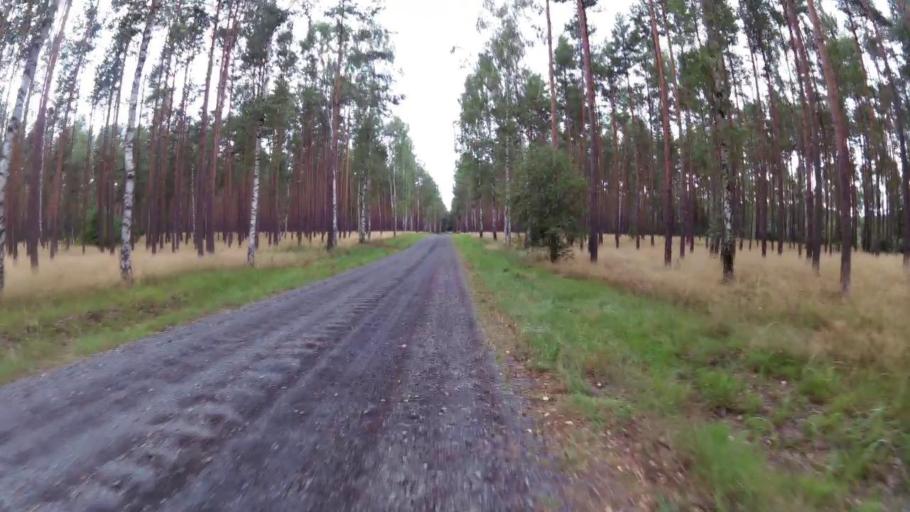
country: PL
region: West Pomeranian Voivodeship
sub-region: Powiat mysliborski
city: Debno
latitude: 52.7931
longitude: 14.7149
